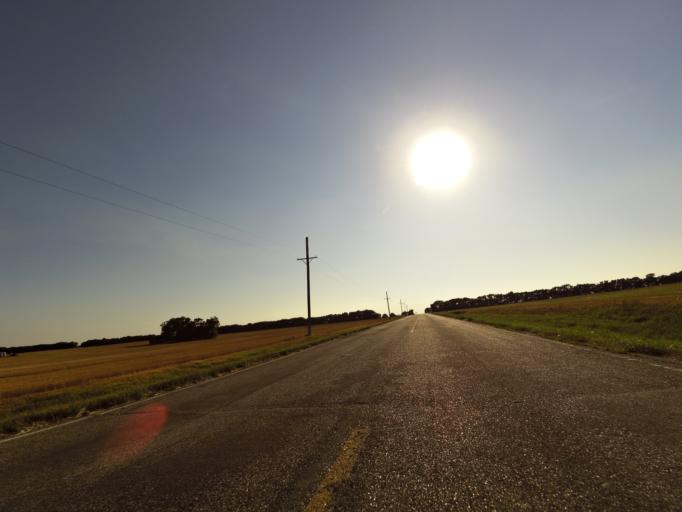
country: US
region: Kansas
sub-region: McPherson County
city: Moundridge
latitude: 38.1451
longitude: -97.5612
